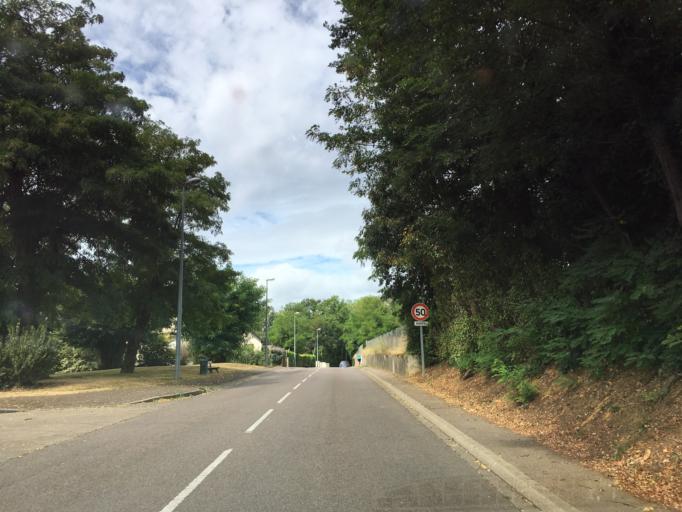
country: FR
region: Bourgogne
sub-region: Departement de l'Yonne
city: Saint-Georges-sur-Baulche
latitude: 47.8012
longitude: 3.5461
